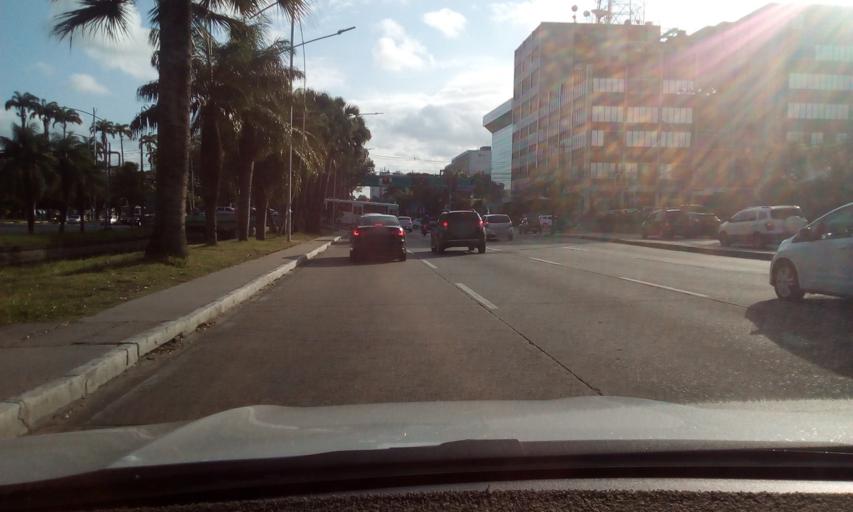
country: BR
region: Pernambuco
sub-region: Recife
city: Recife
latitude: -8.0507
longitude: -34.8947
